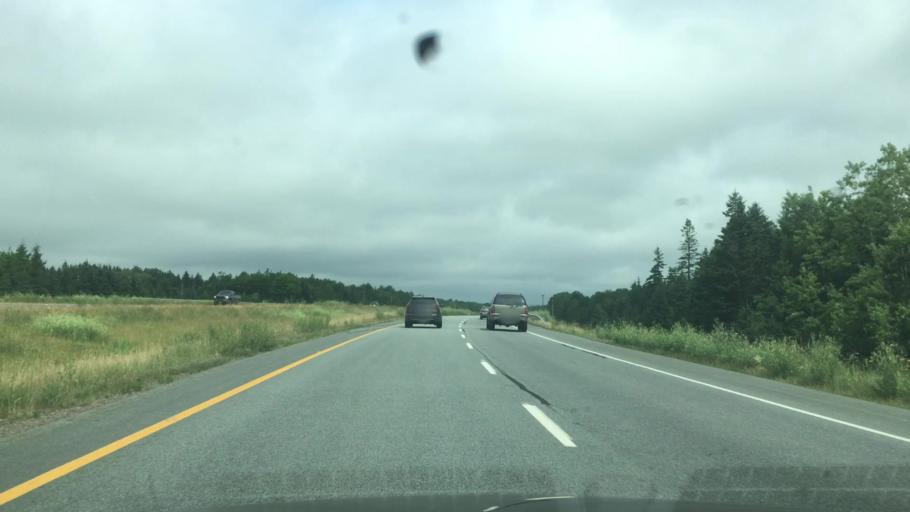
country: CA
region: Nova Scotia
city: Truro
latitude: 45.3017
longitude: -63.3037
